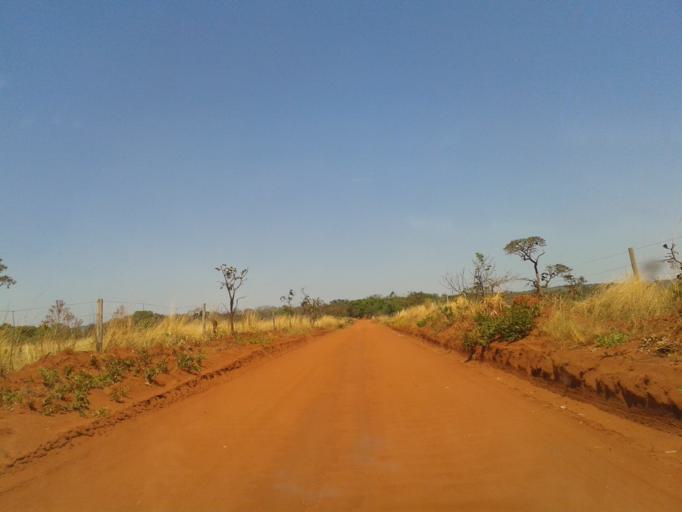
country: BR
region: Minas Gerais
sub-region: Ituiutaba
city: Ituiutaba
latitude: -19.0695
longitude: -49.3388
